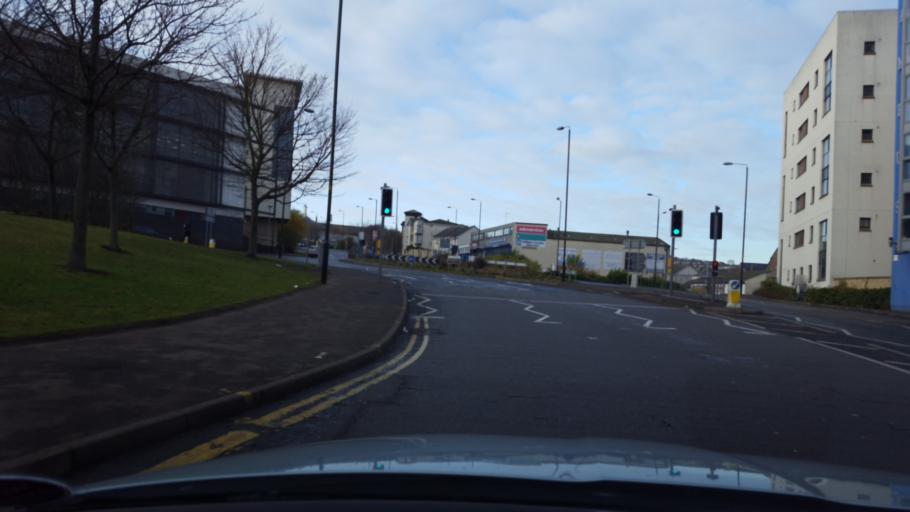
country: GB
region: Scotland
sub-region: Dundee City
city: Dundee
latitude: 56.4600
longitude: -2.9812
